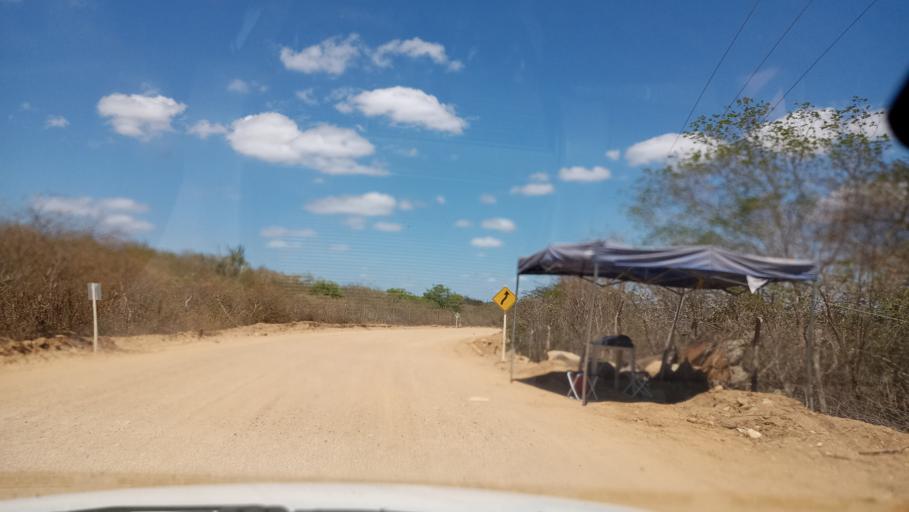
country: BR
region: Rio Grande do Norte
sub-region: Sao Paulo Do Potengi
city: Sao Paulo do Potengi
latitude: -5.7692
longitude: -35.9104
